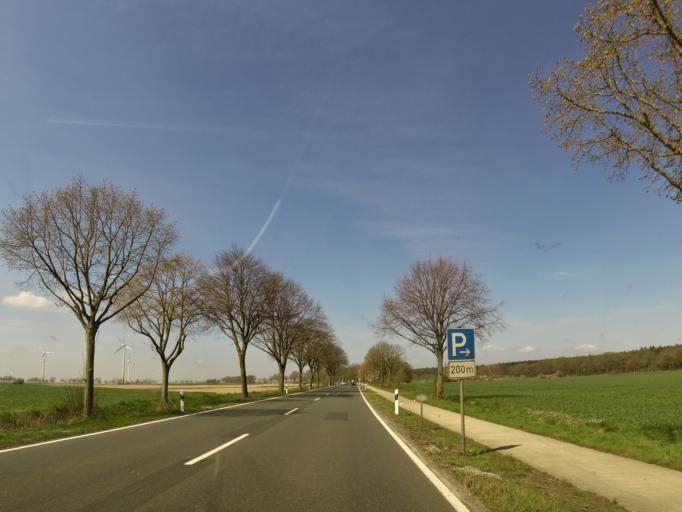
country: DE
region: Lower Saxony
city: Wunstorf
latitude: 52.4303
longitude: 9.3958
